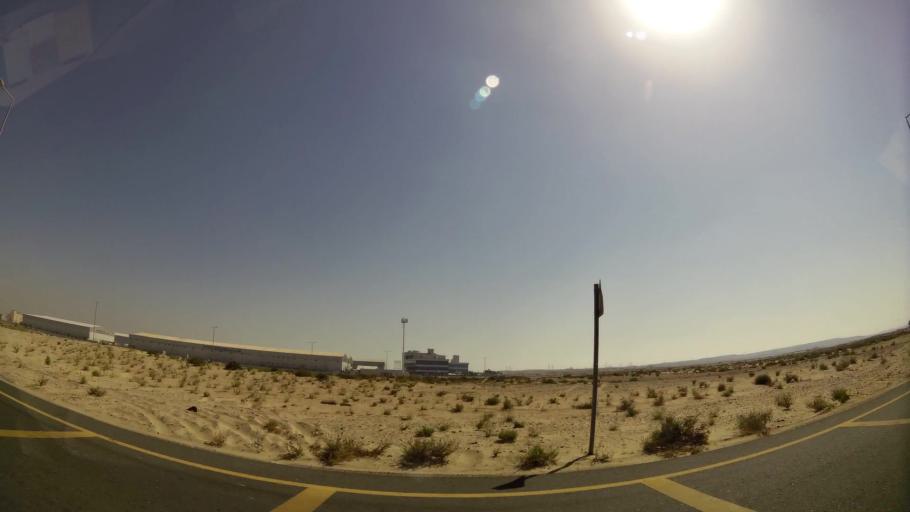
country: AE
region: Dubai
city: Dubai
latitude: 24.9244
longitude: 55.0583
